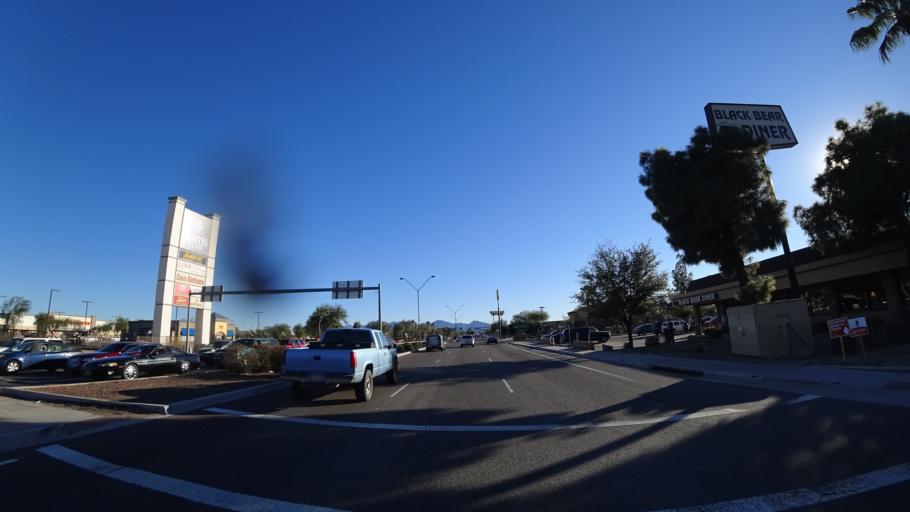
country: US
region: Arizona
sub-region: Maricopa County
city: Avondale
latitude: 33.4572
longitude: -112.3412
